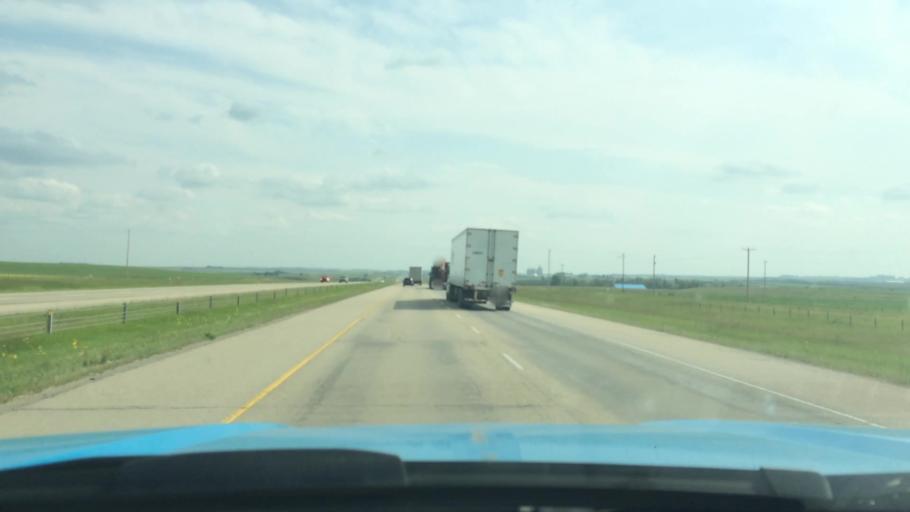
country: CA
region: Alberta
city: Carstairs
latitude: 51.5280
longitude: -114.0251
